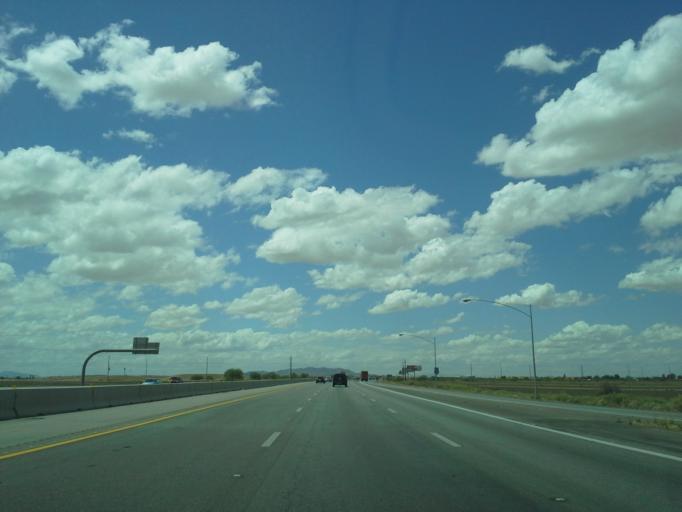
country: US
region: Arizona
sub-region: Pinal County
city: Eloy
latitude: 32.7367
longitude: -111.5535
